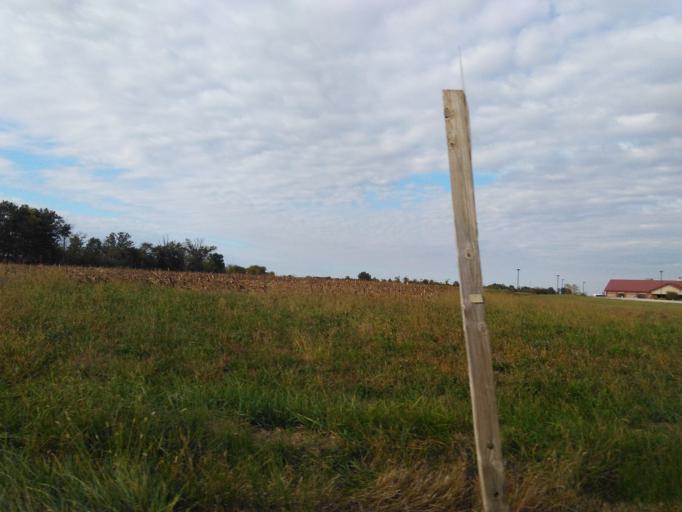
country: US
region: Illinois
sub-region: Bond County
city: Greenville
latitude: 38.9021
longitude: -89.3823
